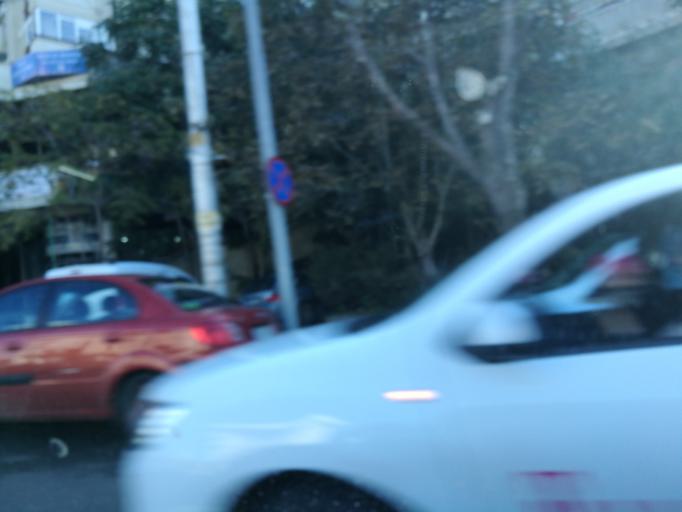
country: RO
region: Iasi
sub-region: Municipiul Iasi
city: Iasi
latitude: 47.1680
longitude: 27.5771
